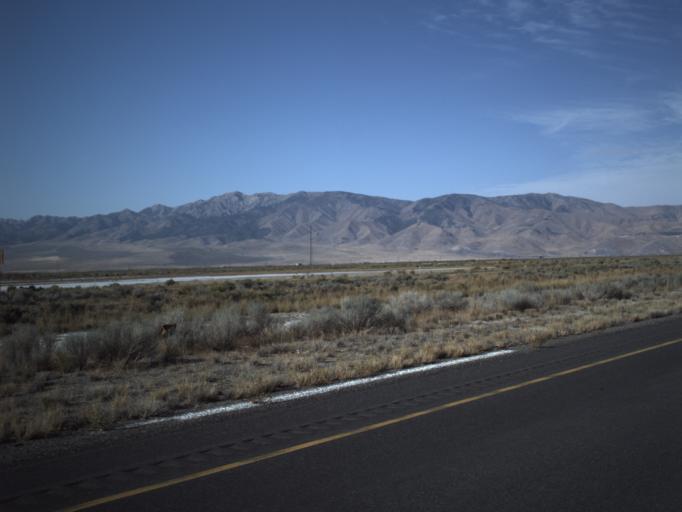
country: US
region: Utah
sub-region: Tooele County
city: Grantsville
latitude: 40.6828
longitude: -112.4314
